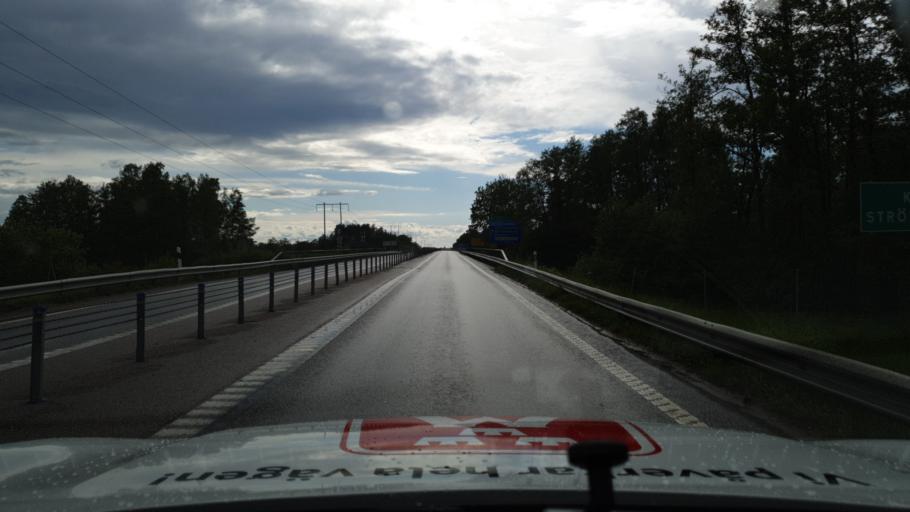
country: SE
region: Vaestmanland
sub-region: Hallstahammars Kommun
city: Hallstahammar
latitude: 59.5922
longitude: 16.2329
